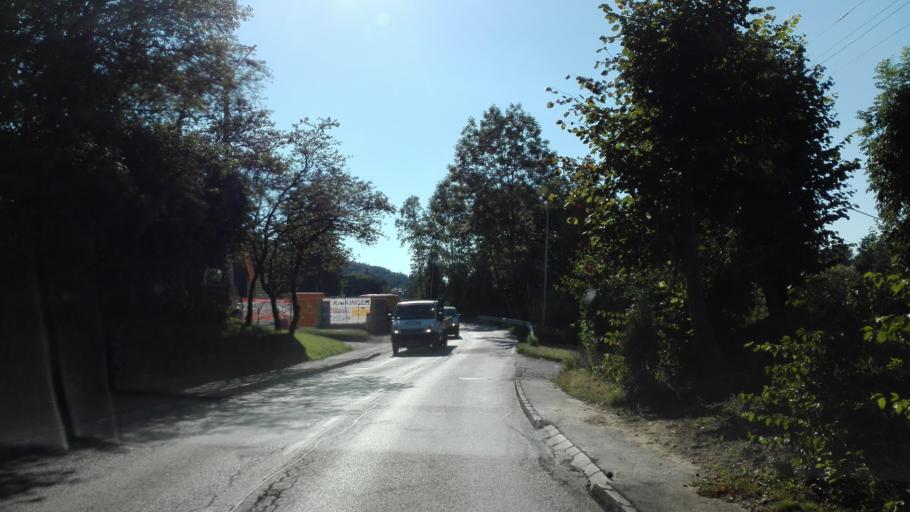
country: AT
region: Lower Austria
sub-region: Politischer Bezirk Sankt Polten
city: Altlengbach
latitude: 48.1527
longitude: 15.9371
